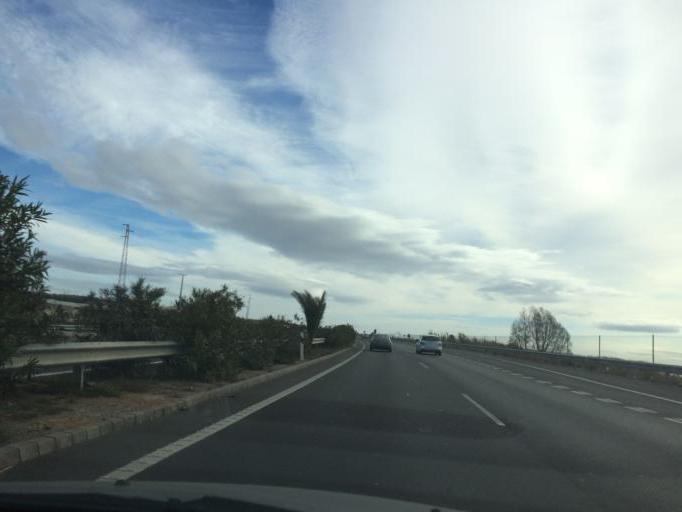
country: ES
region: Andalusia
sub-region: Provincia de Almeria
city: Viator
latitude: 36.8438
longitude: -2.4048
